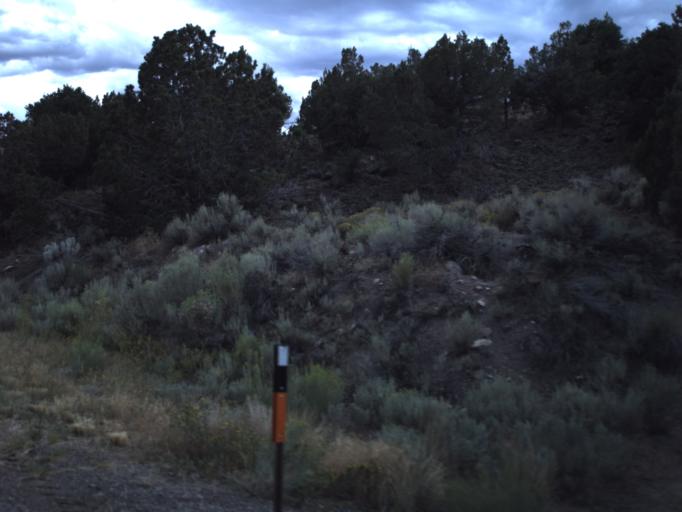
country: US
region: Utah
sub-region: Sevier County
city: Aurora
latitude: 38.7723
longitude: -111.9298
